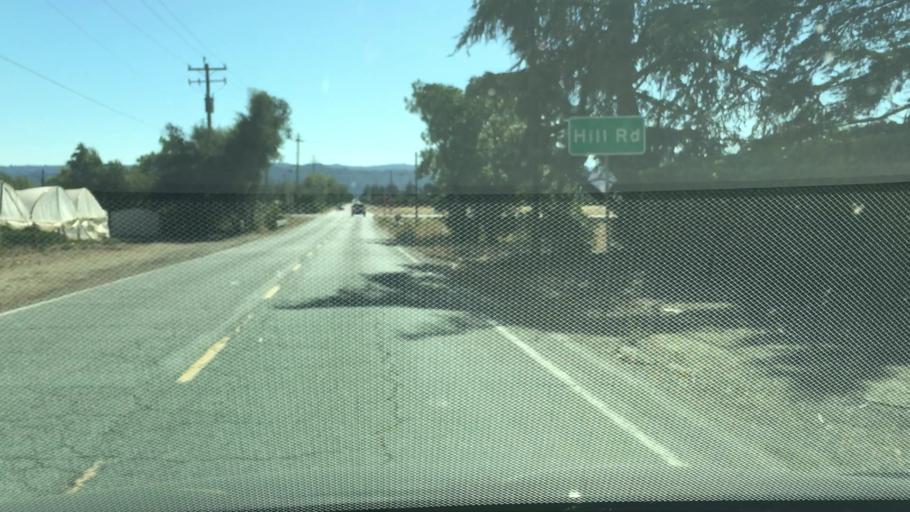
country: US
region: California
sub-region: Santa Clara County
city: San Martin
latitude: 37.1268
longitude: -121.6067
